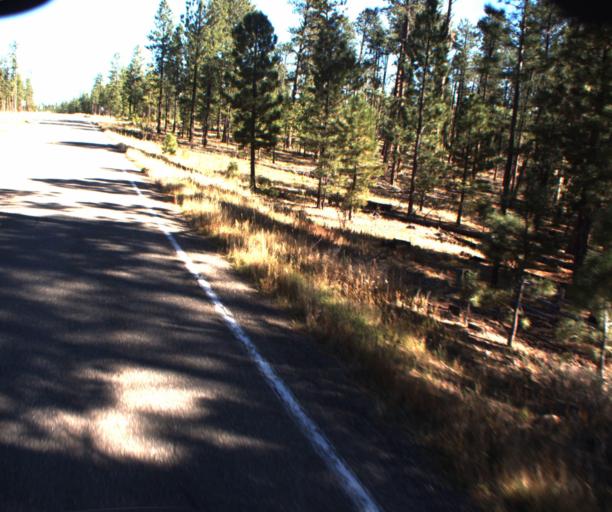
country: US
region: Arizona
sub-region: Coconino County
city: Fredonia
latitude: 36.7193
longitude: -112.2145
